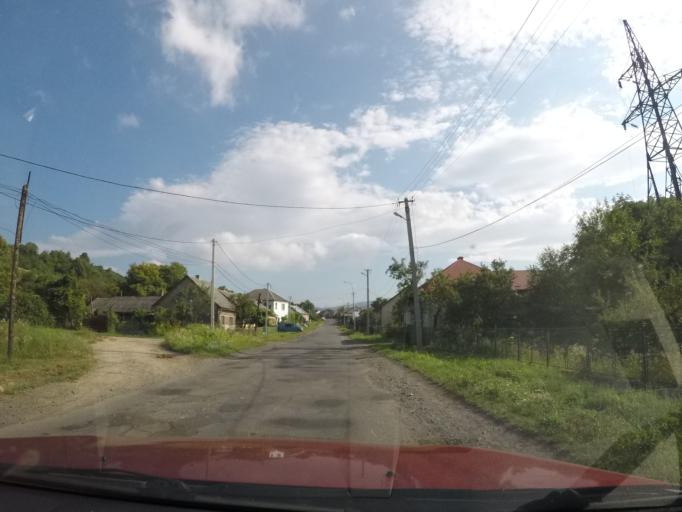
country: UA
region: Zakarpattia
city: Velykyi Bereznyi
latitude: 48.9099
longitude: 22.4594
